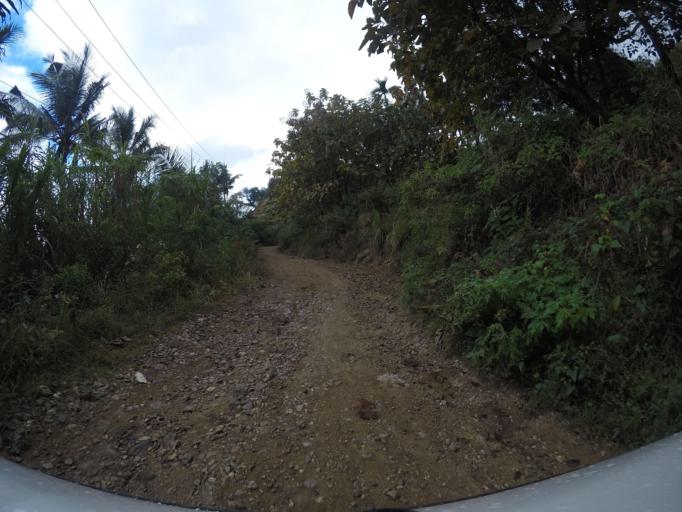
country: TL
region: Baucau
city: Baucau
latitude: -8.6424
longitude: 126.6365
